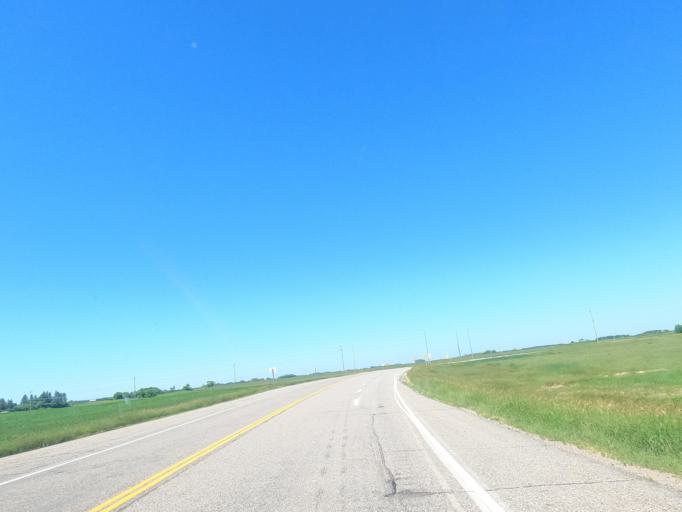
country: CA
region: Manitoba
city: Brandon
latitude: 49.5868
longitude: -99.9590
